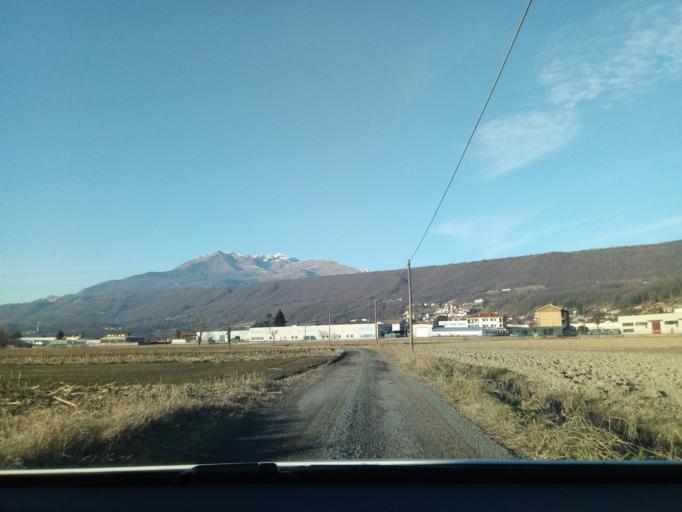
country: IT
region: Piedmont
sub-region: Provincia di Torino
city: Bollengo
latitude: 45.4672
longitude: 7.9326
